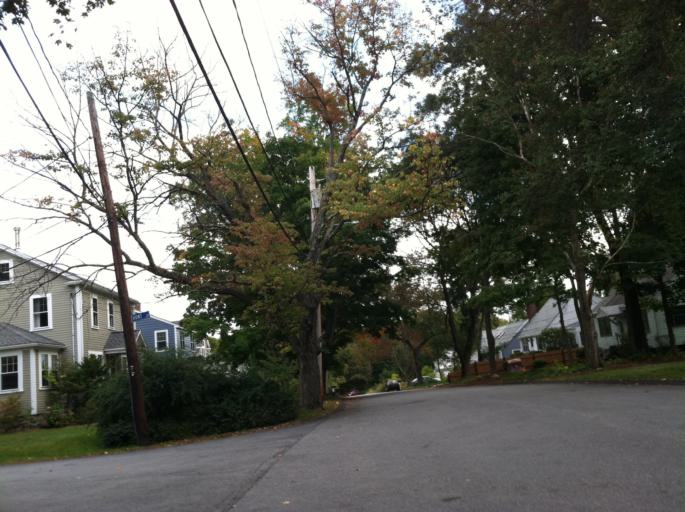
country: US
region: Massachusetts
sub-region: Middlesex County
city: Bedford
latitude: 42.4958
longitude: -71.2777
